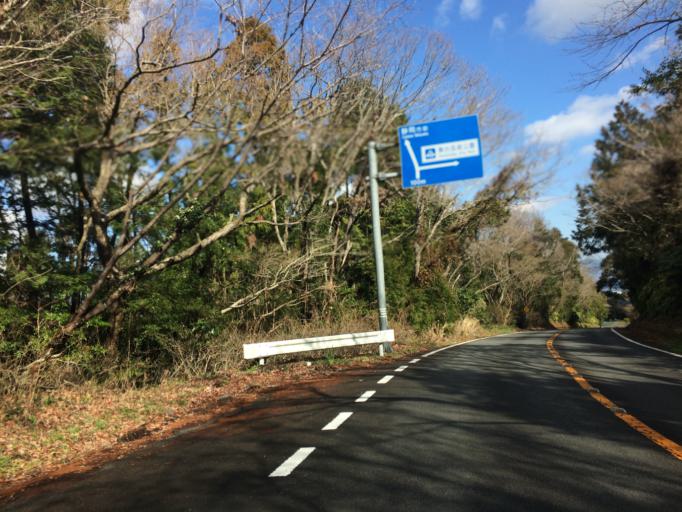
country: JP
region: Shizuoka
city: Shizuoka-shi
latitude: 34.9765
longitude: 138.4471
